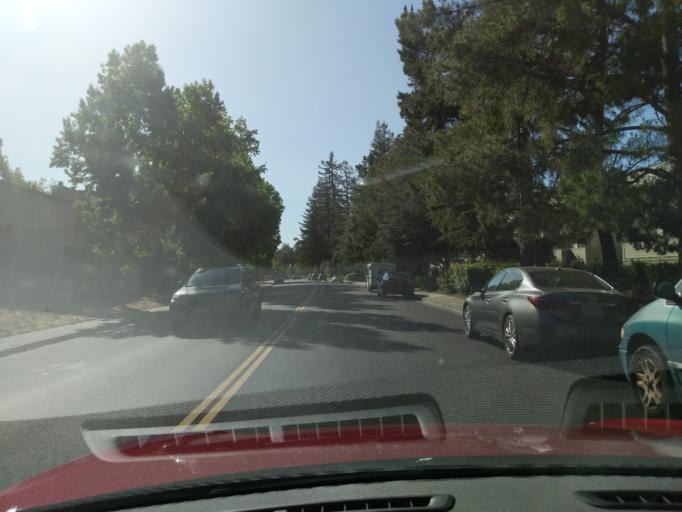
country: US
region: California
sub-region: San Mateo County
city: West Menlo Park
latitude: 37.4265
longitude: -122.1983
